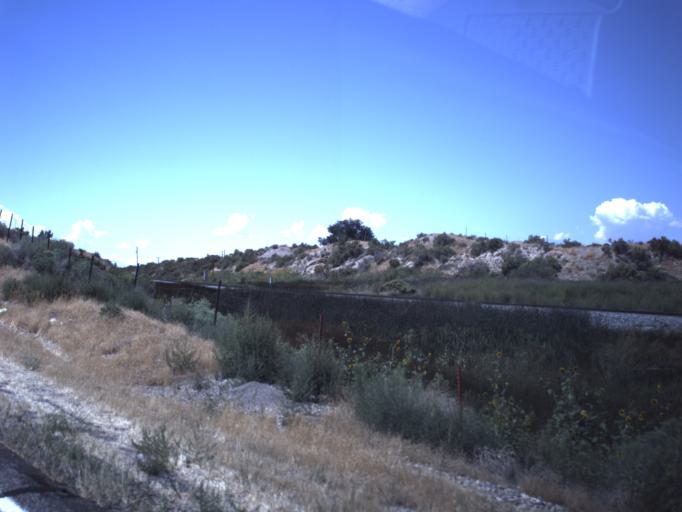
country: US
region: Utah
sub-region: Millard County
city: Delta
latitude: 39.5257
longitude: -112.3634
